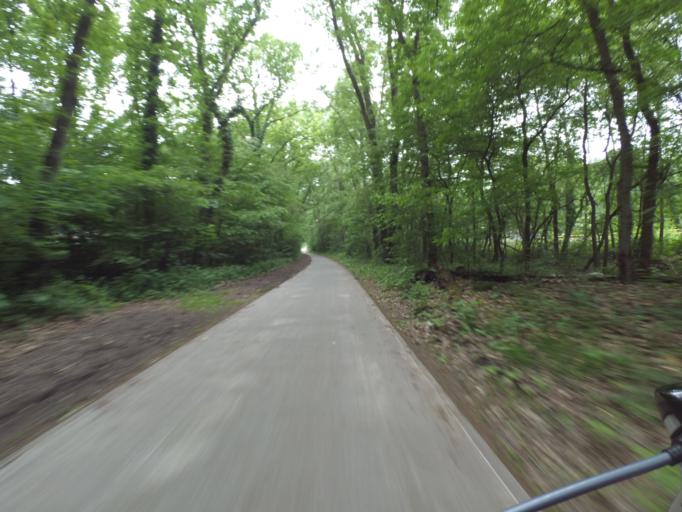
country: NL
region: Gelderland
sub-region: Gemeente Renkum
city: Wolfheze
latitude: 52.0046
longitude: 5.7961
